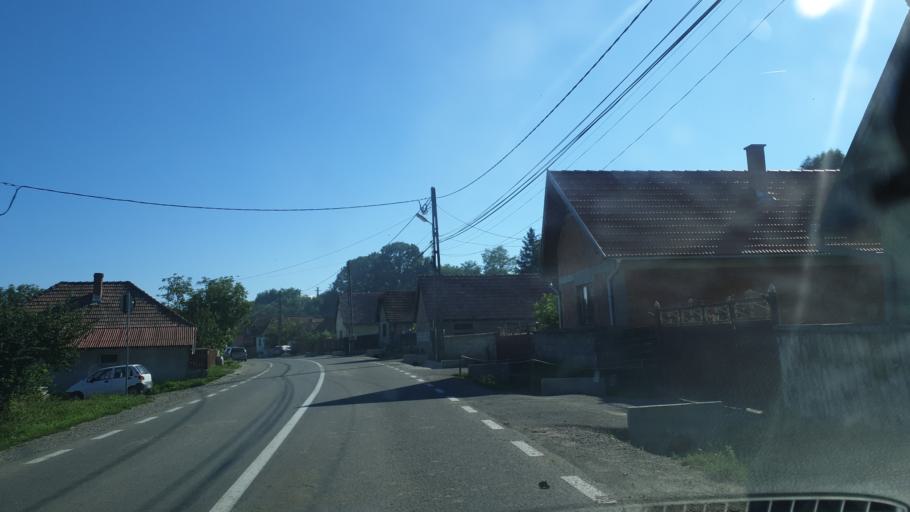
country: RO
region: Covasna
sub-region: Comuna Ilieni
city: Ilieni
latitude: 45.8036
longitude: 25.7695
